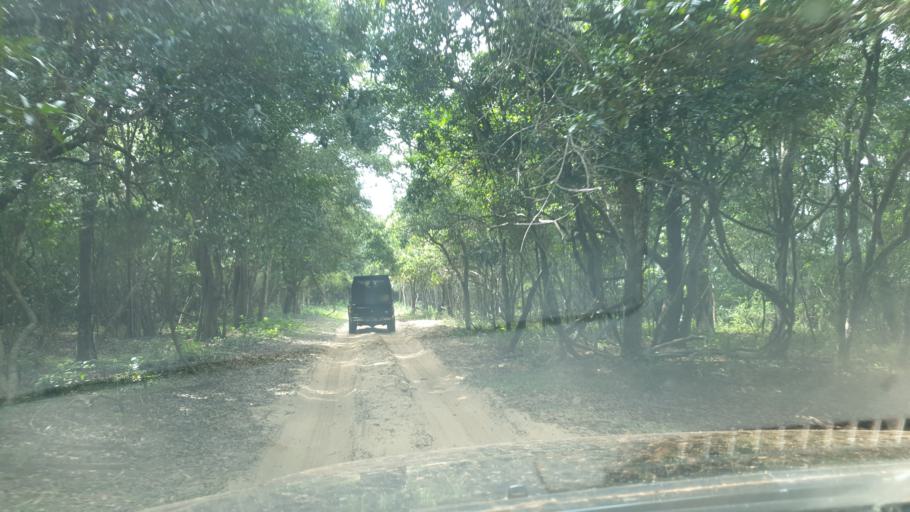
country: LK
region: North Western
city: Puttalam
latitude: 8.4123
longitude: 79.9887
